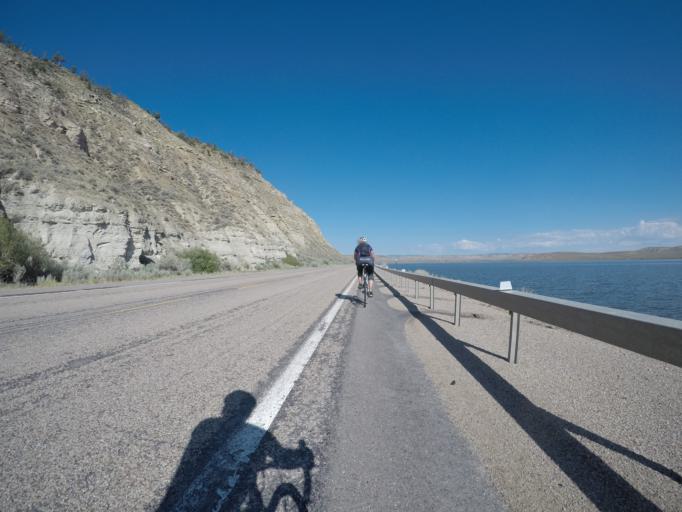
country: US
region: Wyoming
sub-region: Sublette County
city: Marbleton
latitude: 42.1148
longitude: -110.1564
